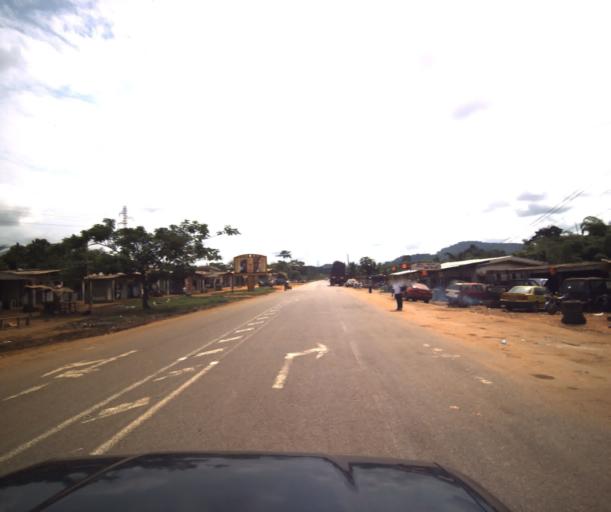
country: CM
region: Centre
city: Eseka
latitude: 3.8546
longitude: 10.5255
